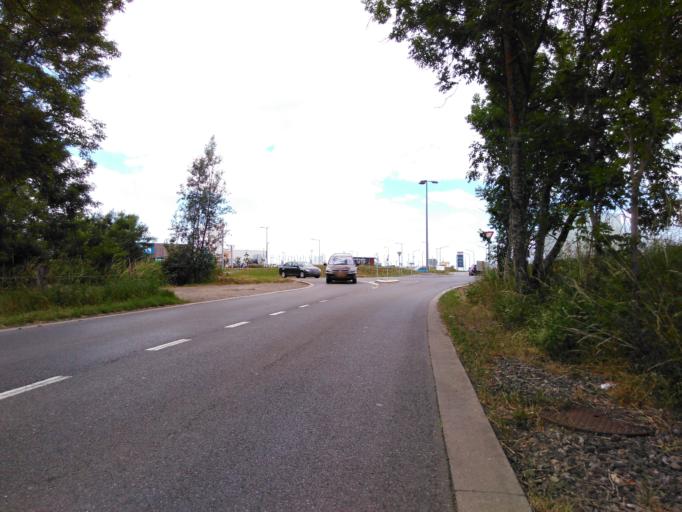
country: LU
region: Luxembourg
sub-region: Canton de Capellen
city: Steinfort
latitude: 49.6362
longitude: 5.8875
